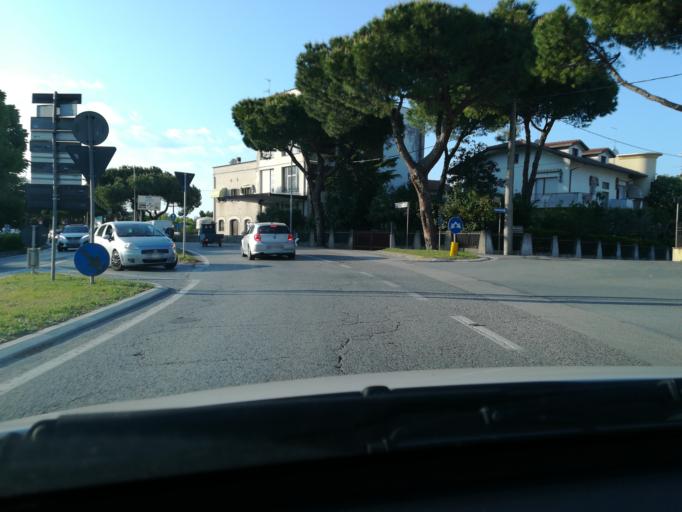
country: IT
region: Emilia-Romagna
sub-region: Provincia di Rimini
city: Riccione
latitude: 43.9975
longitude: 12.6482
